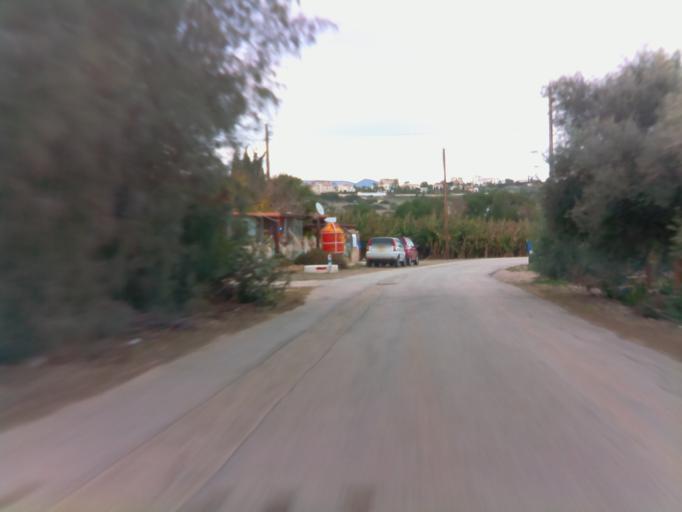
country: CY
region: Pafos
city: Pegeia
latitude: 34.8769
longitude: 32.3417
